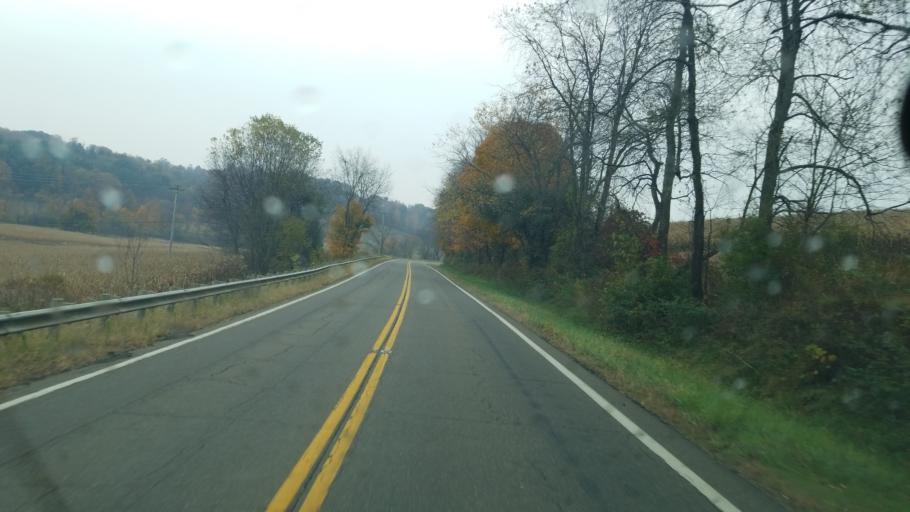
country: US
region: Ohio
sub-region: Holmes County
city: Millersburg
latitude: 40.4621
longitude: -81.9025
